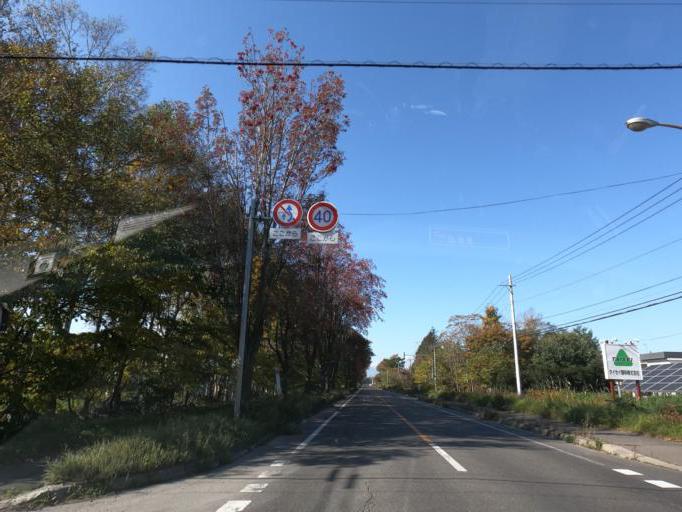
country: JP
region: Hokkaido
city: Obihiro
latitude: 42.9444
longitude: 143.2366
